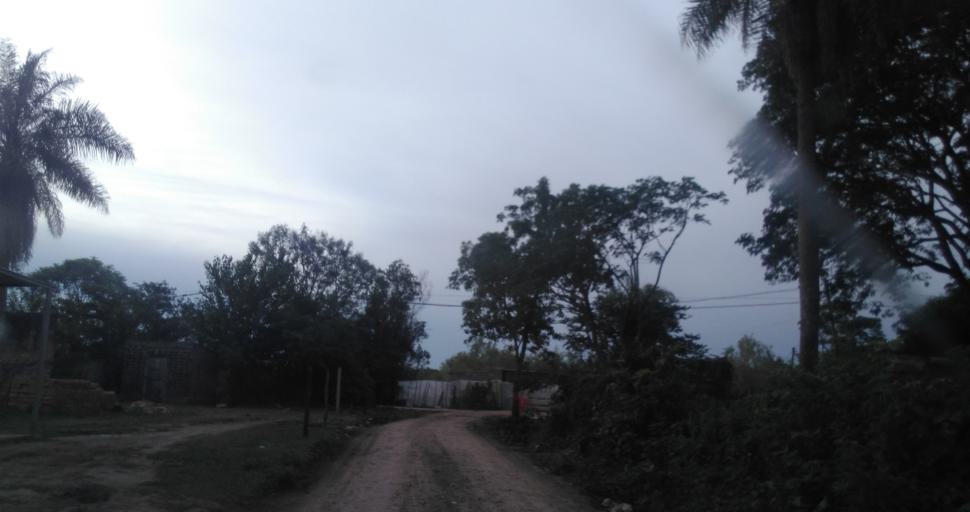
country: AR
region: Chaco
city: Fontana
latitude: -27.4091
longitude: -59.0268
